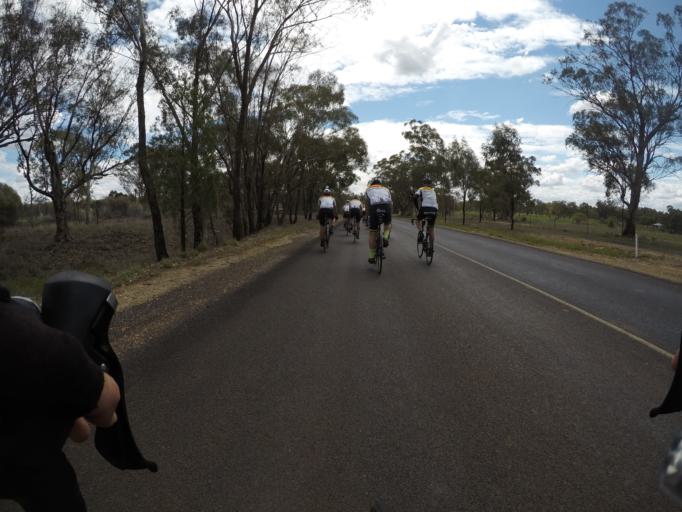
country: AU
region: New South Wales
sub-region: Dubbo Municipality
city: Dubbo
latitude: -32.2821
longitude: 148.5947
